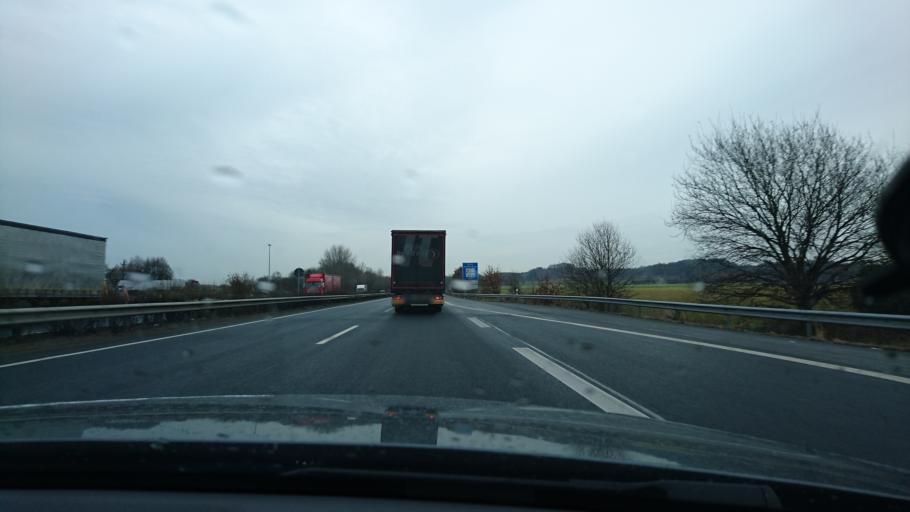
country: DE
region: Lower Saxony
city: Neuenkirchen
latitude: 52.4957
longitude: 8.0771
